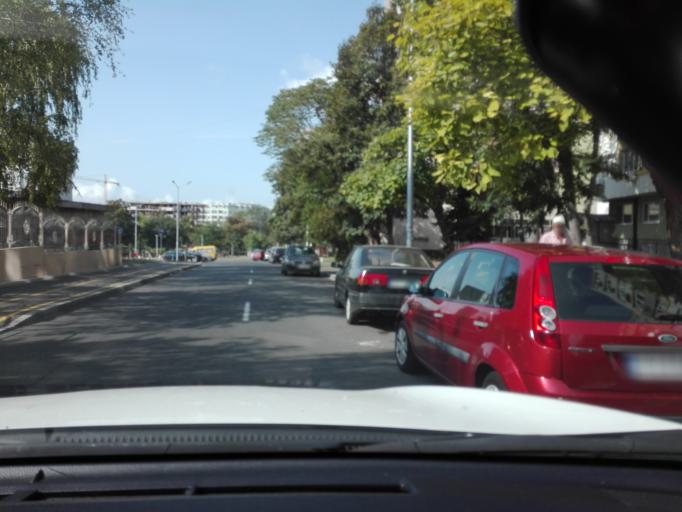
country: BG
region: Burgas
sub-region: Obshtina Burgas
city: Burgas
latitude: 42.4576
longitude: 27.4193
